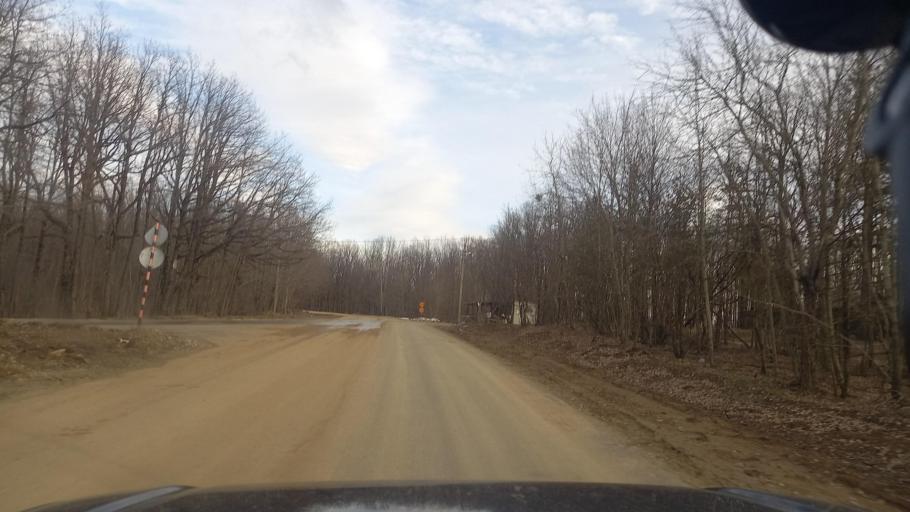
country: RU
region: Krasnodarskiy
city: Goryachiy Klyuch
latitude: 44.6993
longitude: 39.0220
